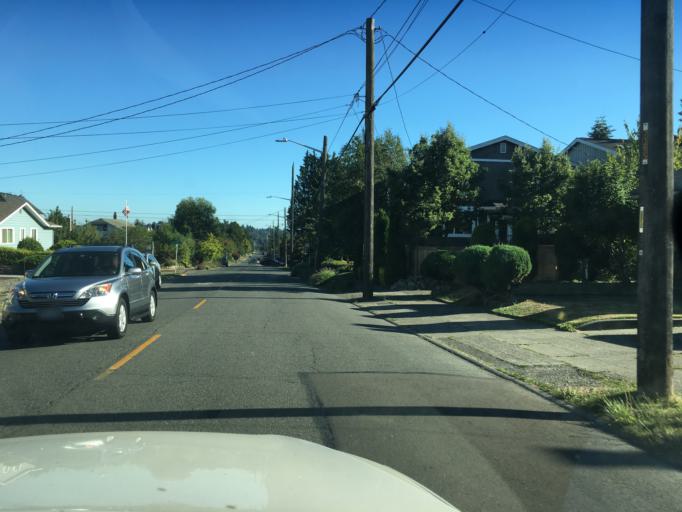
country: US
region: Washington
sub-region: King County
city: Shoreline
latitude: 47.6825
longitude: -122.3984
